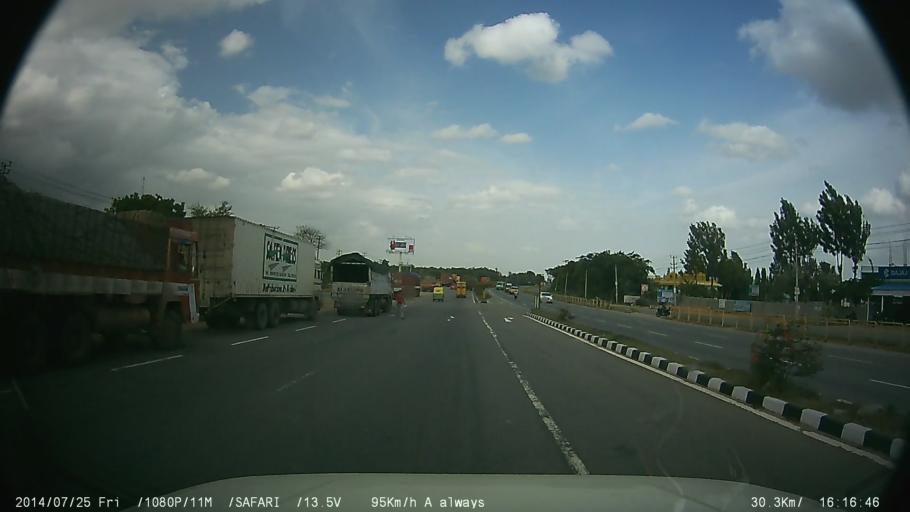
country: IN
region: Tamil Nadu
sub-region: Krishnagiri
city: Hosur
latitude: 12.7836
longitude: 77.7571
